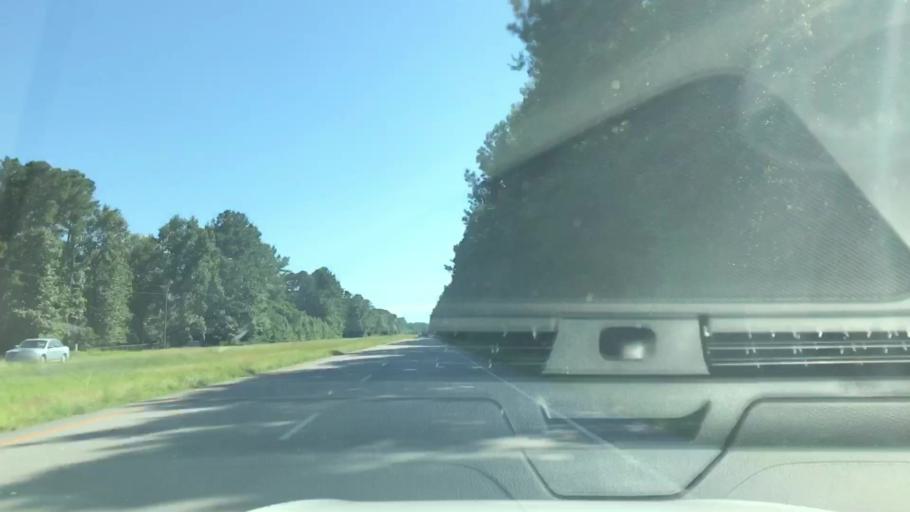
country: US
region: South Carolina
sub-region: Charleston County
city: Awendaw
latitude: 33.1155
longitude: -79.4570
